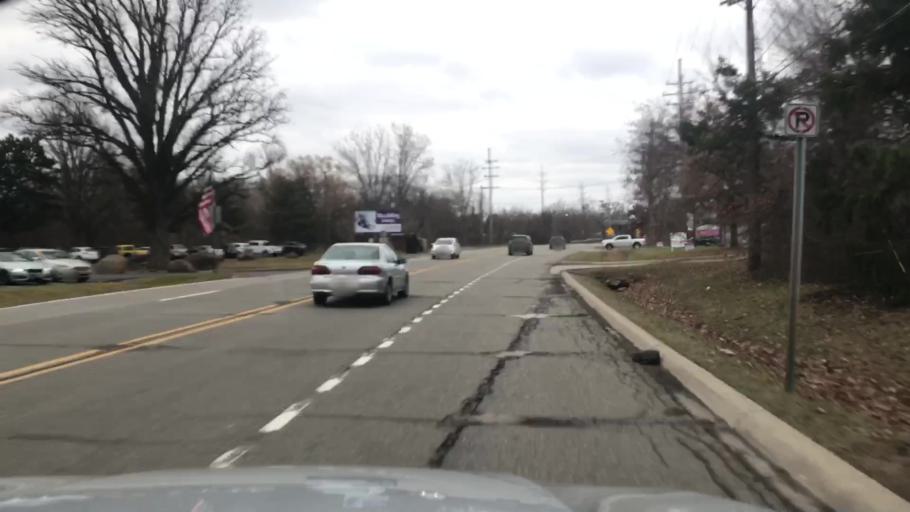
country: US
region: Michigan
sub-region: Wayne County
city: Northville
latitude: 42.4444
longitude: -83.4738
